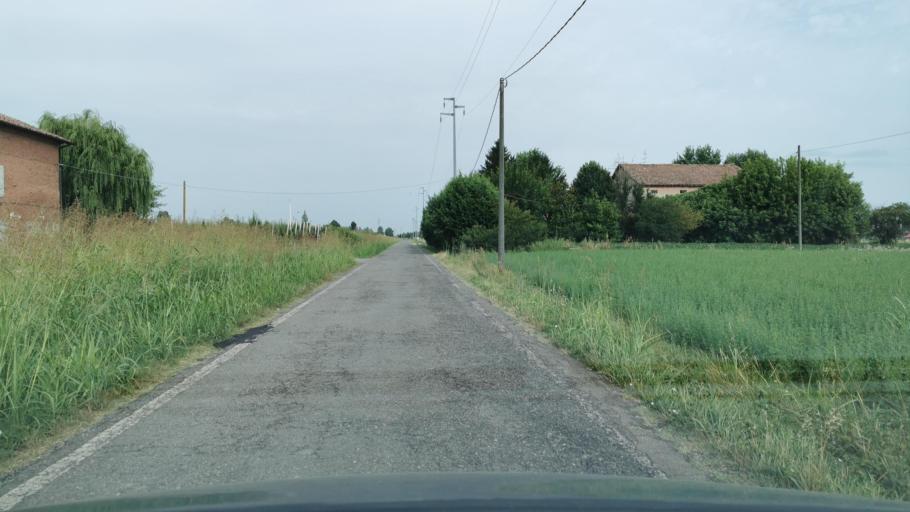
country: IT
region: Emilia-Romagna
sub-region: Provincia di Modena
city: Villanova
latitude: 44.6866
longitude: 10.9050
